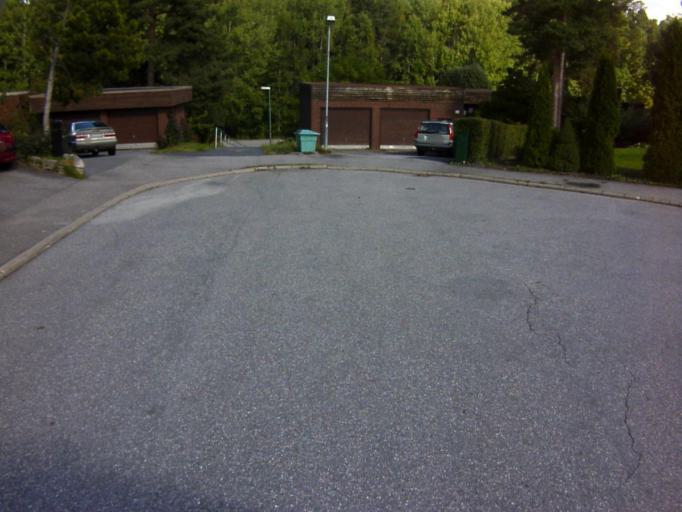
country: SE
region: Soedermanland
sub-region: Eskilstuna Kommun
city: Eskilstuna
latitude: 59.3984
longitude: 16.5380
